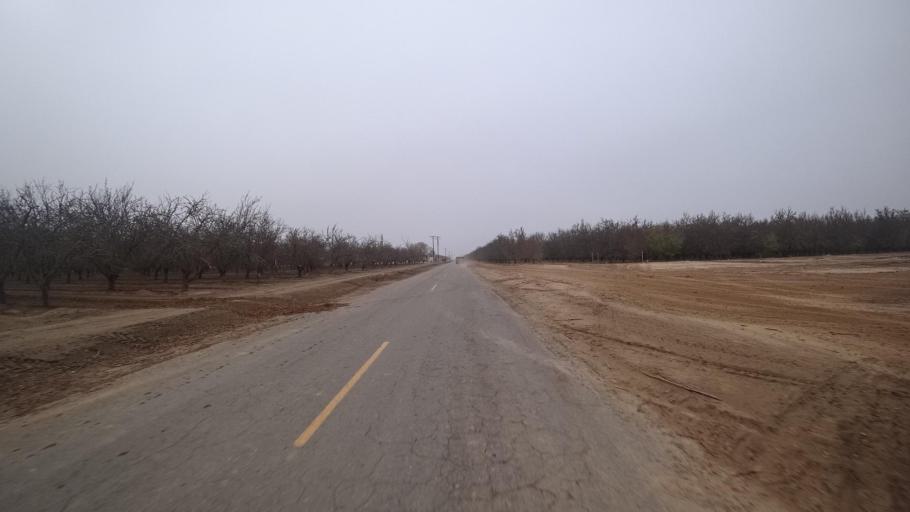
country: US
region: California
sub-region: Kern County
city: Lost Hills
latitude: 35.5796
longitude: -119.5271
